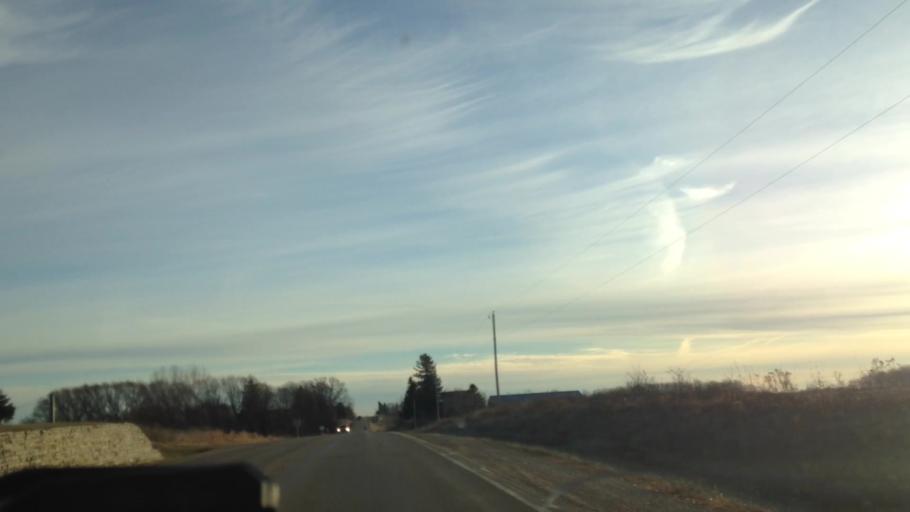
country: US
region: Wisconsin
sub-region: Dodge County
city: Theresa
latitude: 43.5366
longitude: -88.4798
